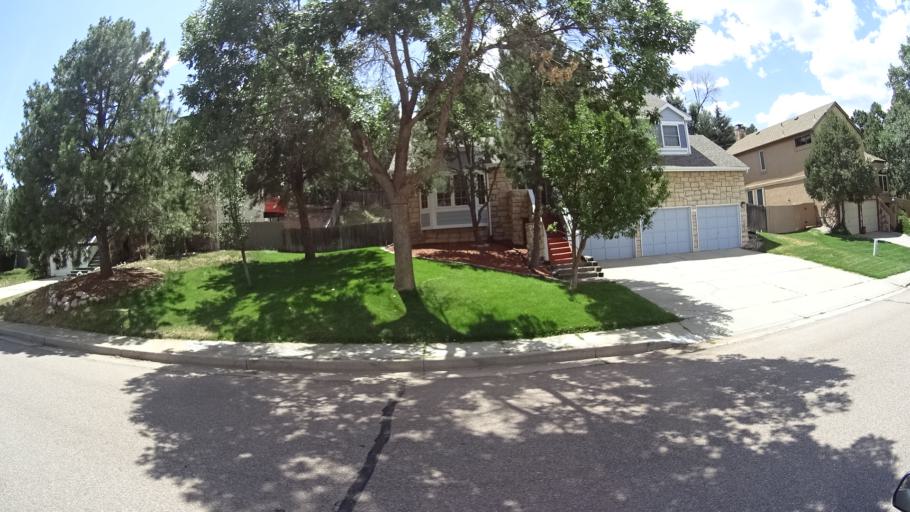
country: US
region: Colorado
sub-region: El Paso County
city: Air Force Academy
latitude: 38.9397
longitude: -104.8419
